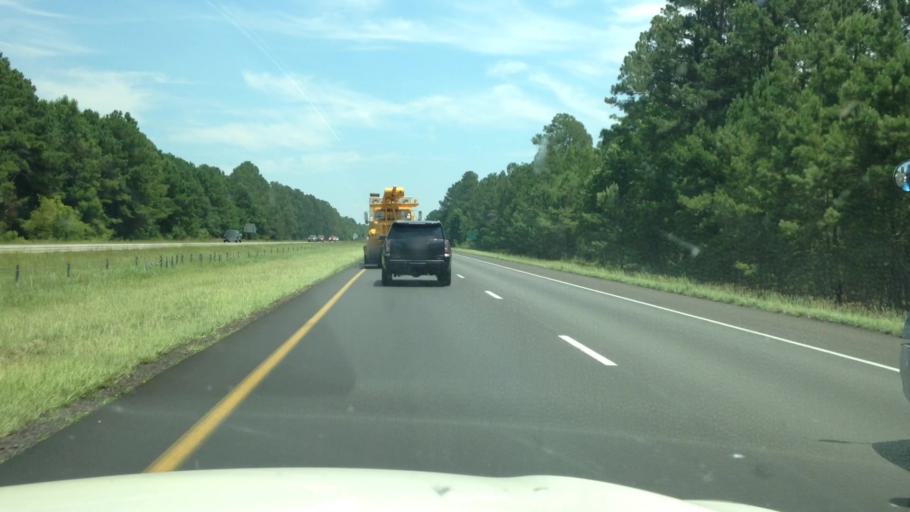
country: US
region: South Carolina
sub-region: Florence County
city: Timmonsville
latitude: 34.2052
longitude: -80.0138
